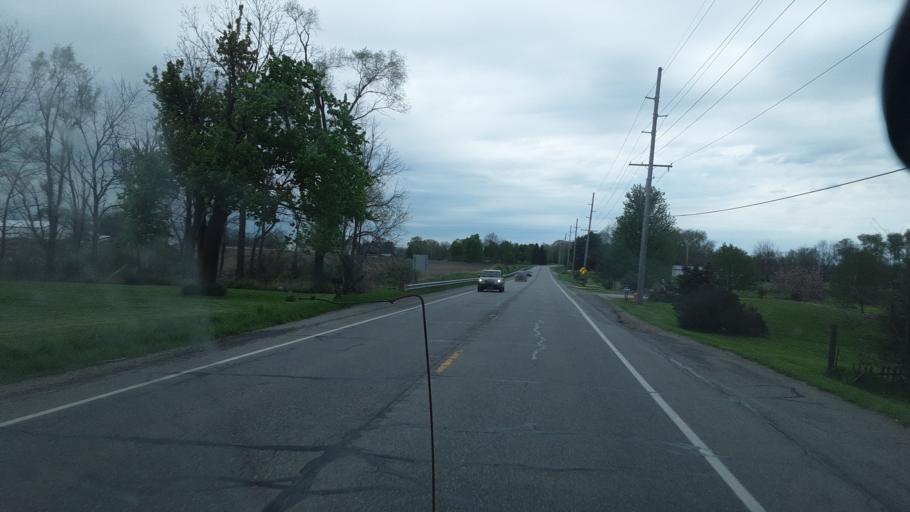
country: US
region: Indiana
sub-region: Elkhart County
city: Goshen
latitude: 41.6234
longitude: -85.8305
